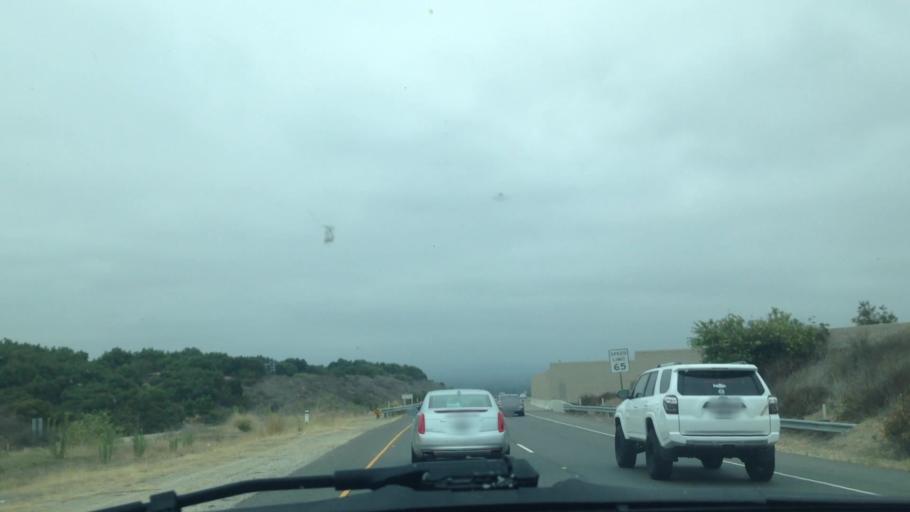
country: US
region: California
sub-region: Orange County
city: North Tustin
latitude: 33.7636
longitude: -117.7593
